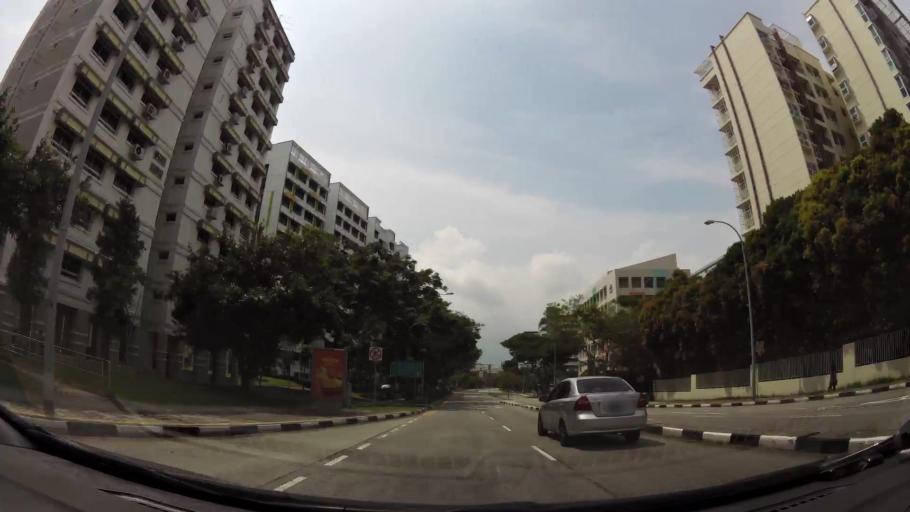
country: MY
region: Johor
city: Kampung Pasir Gudang Baru
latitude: 1.3689
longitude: 103.9603
